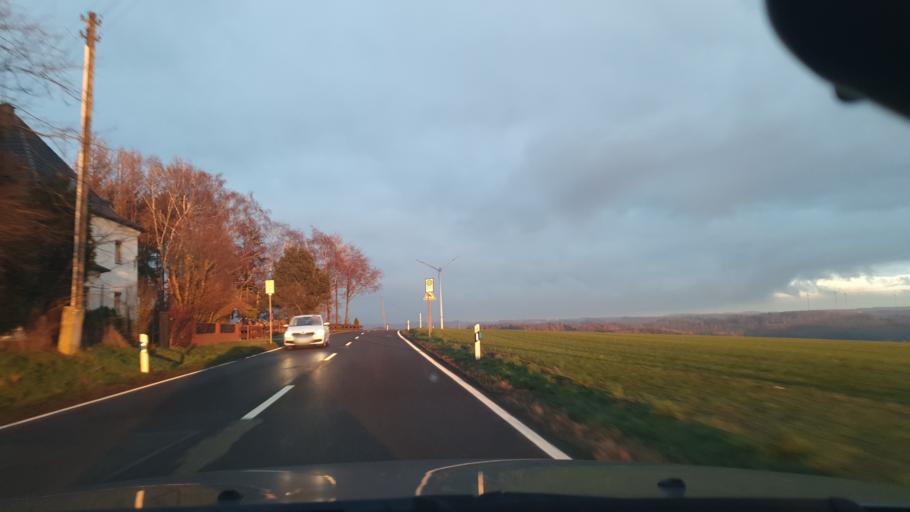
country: DE
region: Rheinland-Pfalz
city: Martinshohe
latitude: 49.3649
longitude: 7.5008
